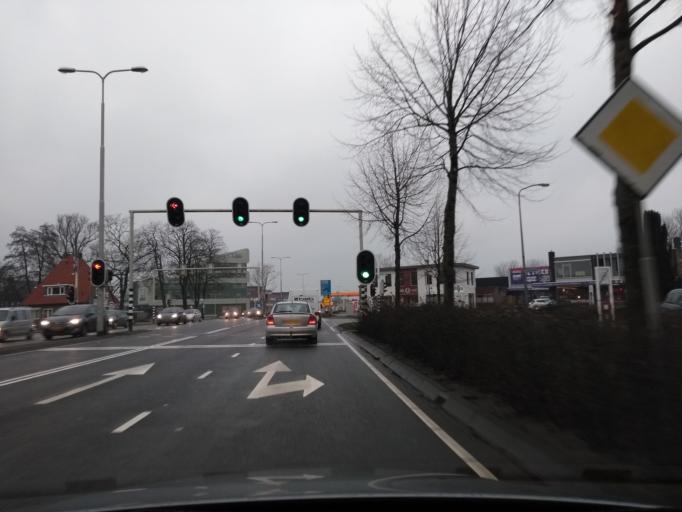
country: NL
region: Overijssel
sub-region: Gemeente Hardenberg
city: Hardenberg
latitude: 52.5734
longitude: 6.6042
